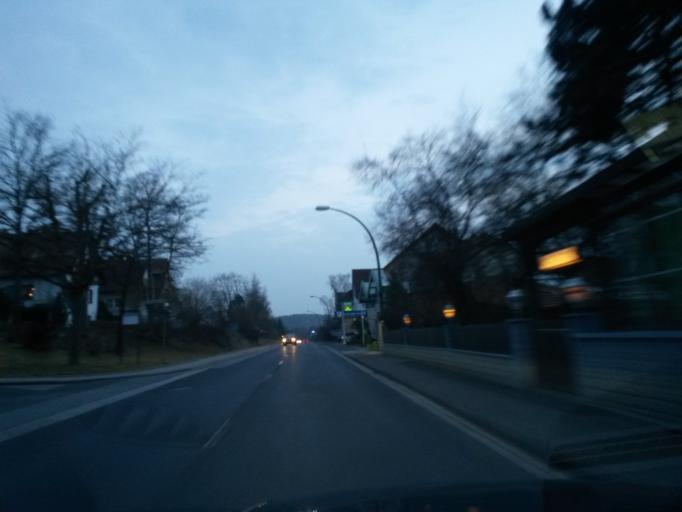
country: DE
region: Bavaria
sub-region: Regierungsbezirk Unterfranken
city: Stadtlauringen
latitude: 50.1857
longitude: 10.3590
